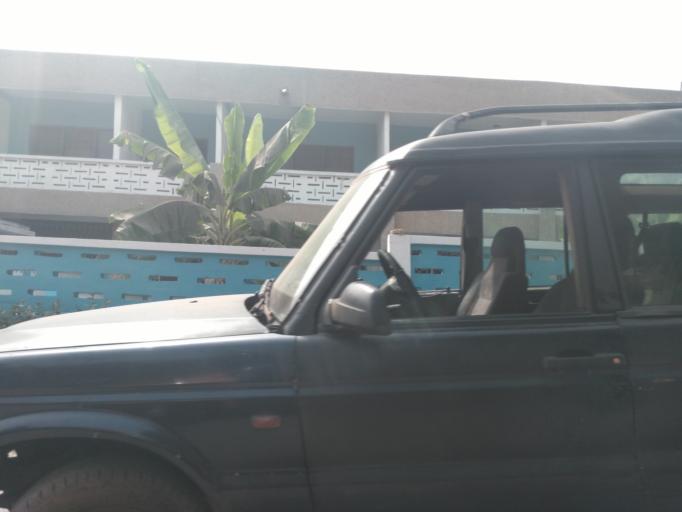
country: GH
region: Ashanti
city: Kumasi
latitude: 6.6793
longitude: -1.6019
